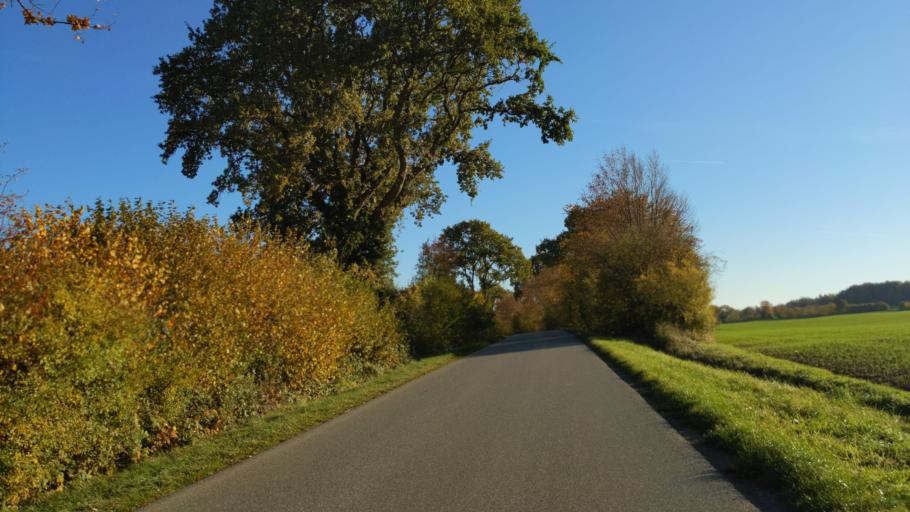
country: DE
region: Schleswig-Holstein
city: Einhaus
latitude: 53.7257
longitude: 10.7191
